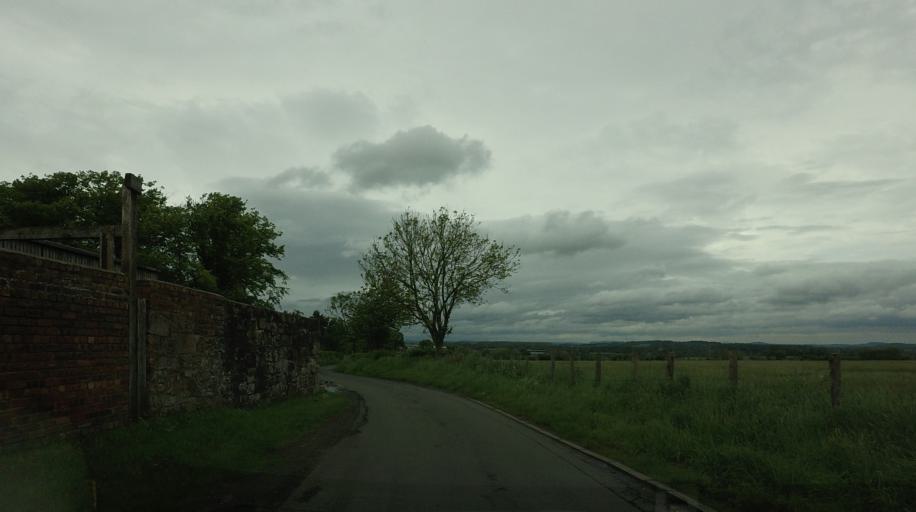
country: GB
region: Scotland
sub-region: West Lothian
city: Broxburn
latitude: 55.9216
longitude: -3.4442
